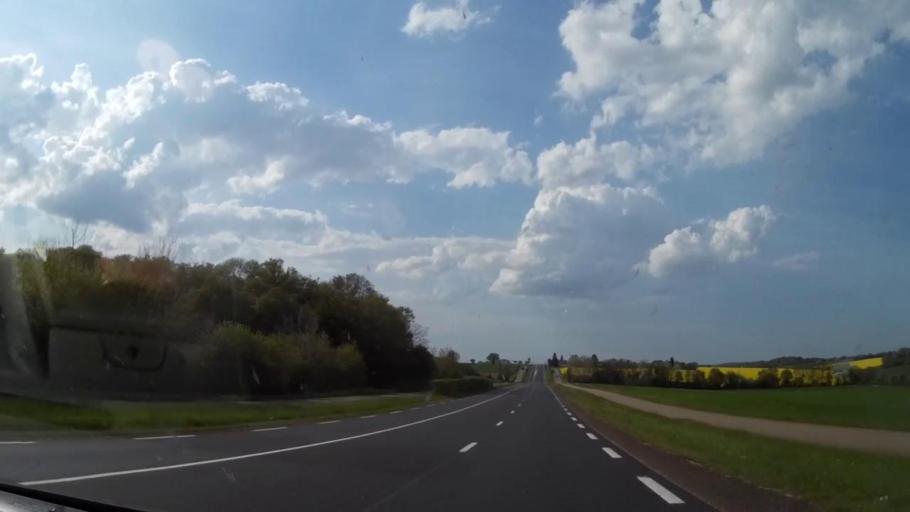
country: FR
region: Centre
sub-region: Departement du Loir-et-Cher
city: Aze
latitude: 47.8791
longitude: 0.9563
